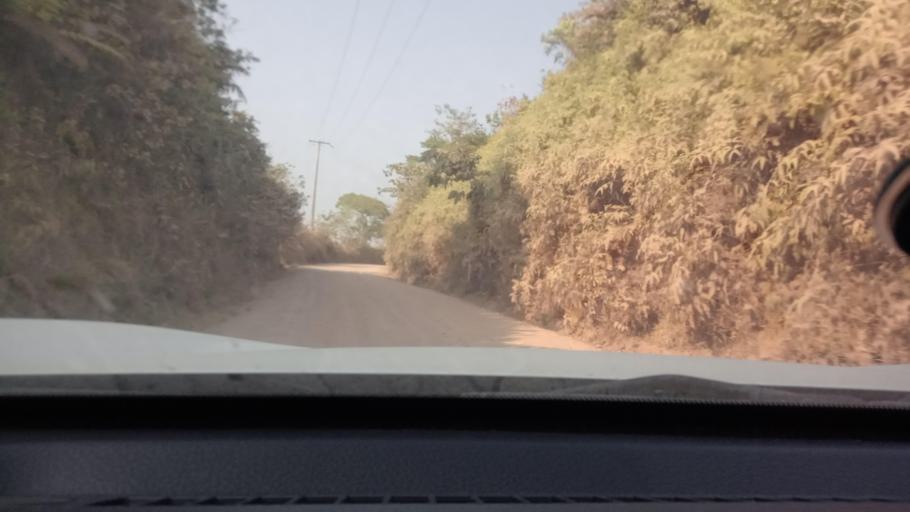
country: MX
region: Tabasco
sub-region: Huimanguillo
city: Francisco Rueda
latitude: 17.6532
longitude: -93.8817
